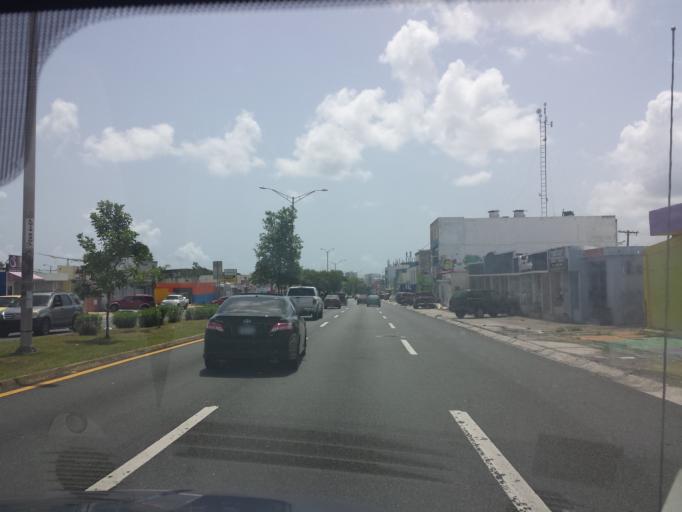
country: PR
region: Catano
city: Catano
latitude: 18.4025
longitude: -66.0896
